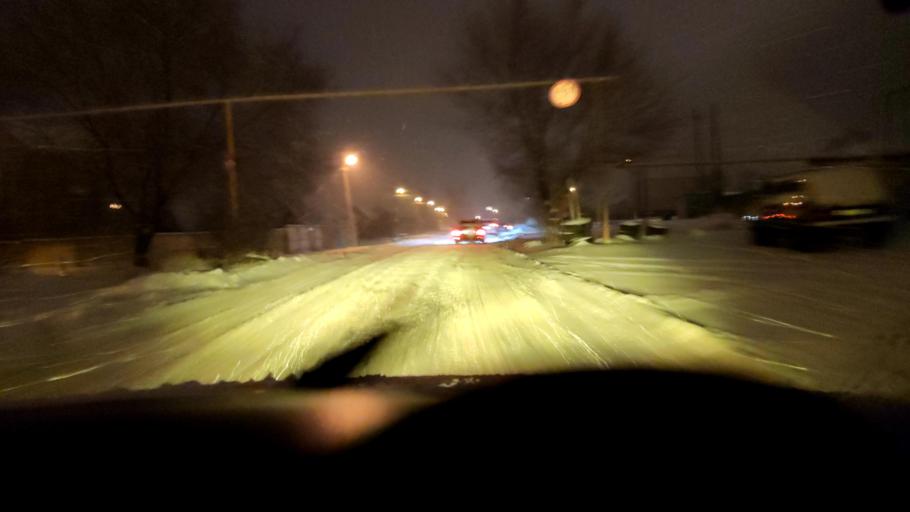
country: RU
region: Voronezj
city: Pridonskoy
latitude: 51.6725
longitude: 39.0776
